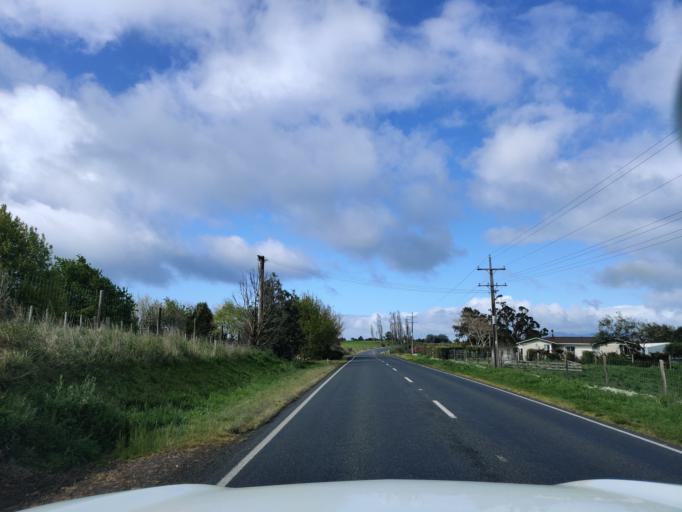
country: NZ
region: Waikato
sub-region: Hamilton City
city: Hamilton
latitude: -37.8360
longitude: 175.2168
